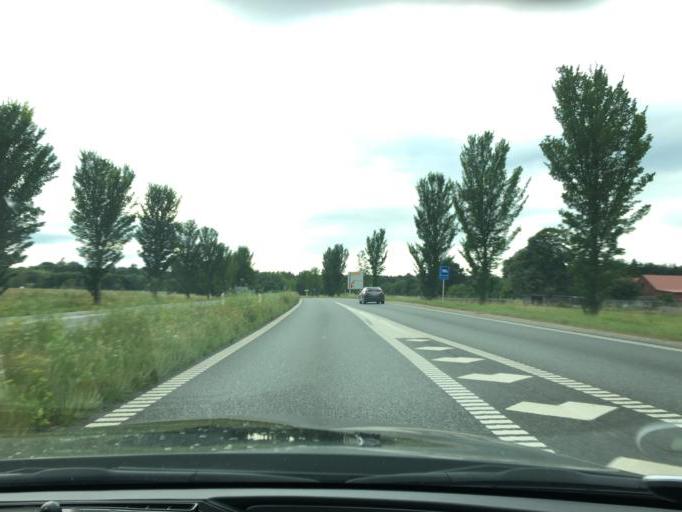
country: DK
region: Capital Region
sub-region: Hillerod Kommune
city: Hillerod
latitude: 55.9521
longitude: 12.3176
